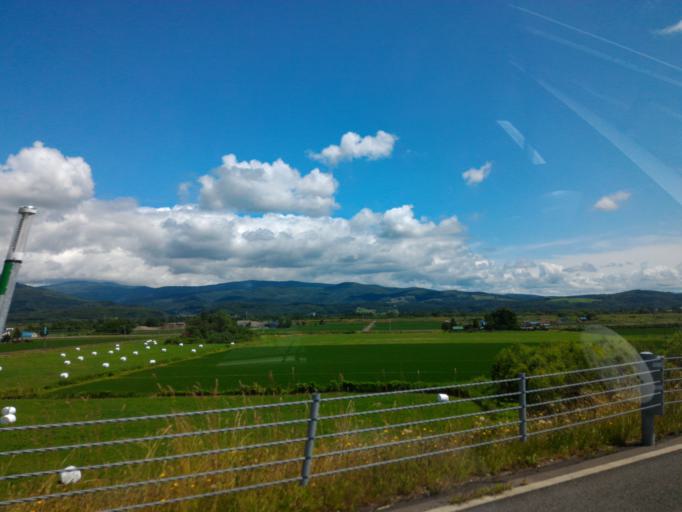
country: JP
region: Hokkaido
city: Nayoro
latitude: 44.3750
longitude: 142.4304
